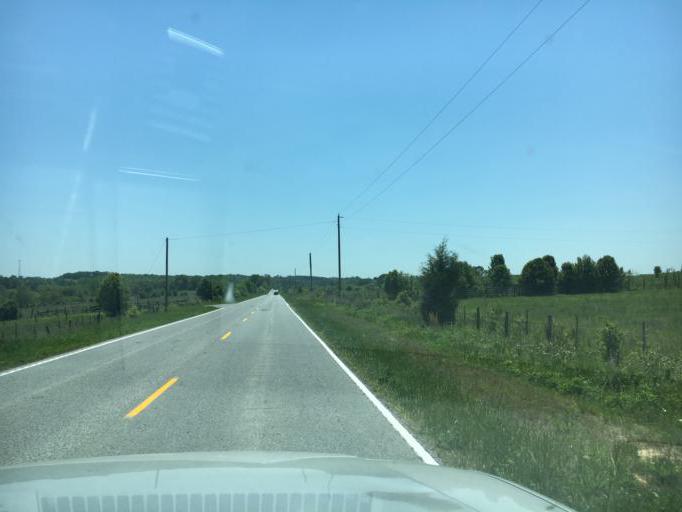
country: US
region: South Carolina
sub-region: Cherokee County
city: Blacksburg
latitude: 35.1696
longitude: -81.5735
